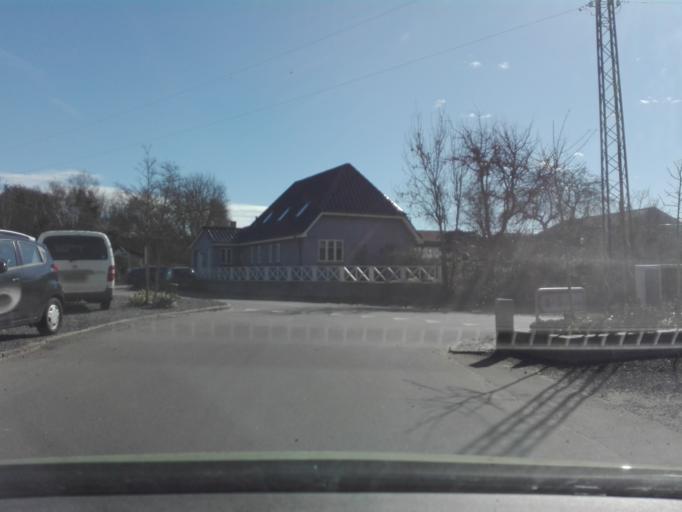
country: DK
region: Central Jutland
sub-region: Horsens Kommune
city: Horsens
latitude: 55.8892
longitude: 9.9558
